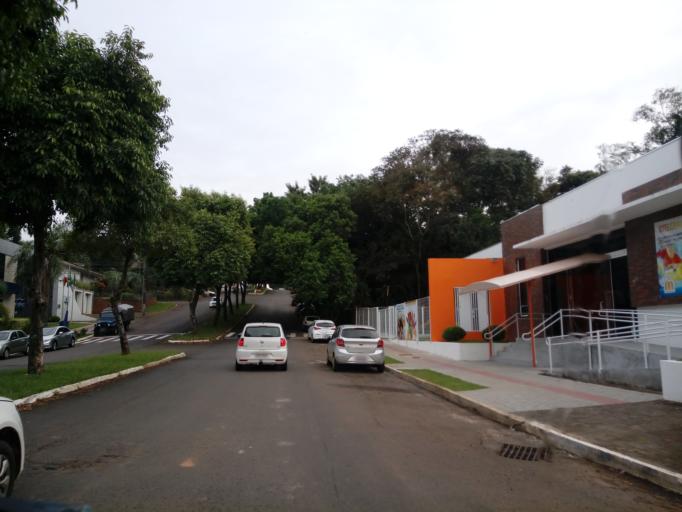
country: BR
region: Santa Catarina
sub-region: Chapeco
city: Chapeco
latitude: -27.0963
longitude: -52.6069
